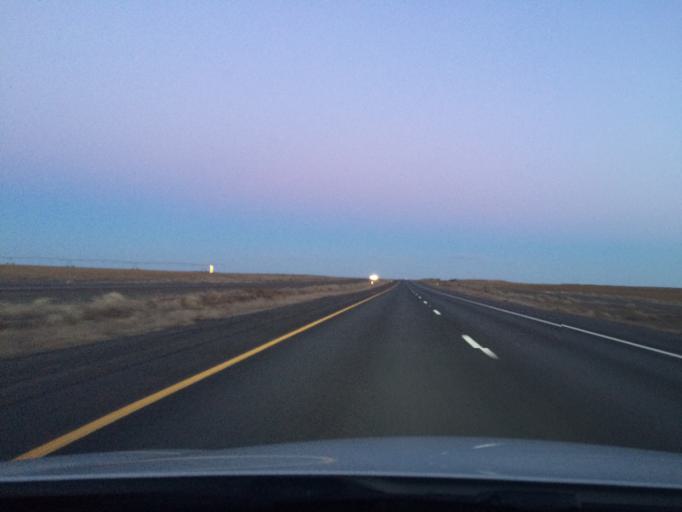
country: US
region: Washington
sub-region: Grant County
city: Quincy
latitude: 47.1036
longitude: -119.6933
